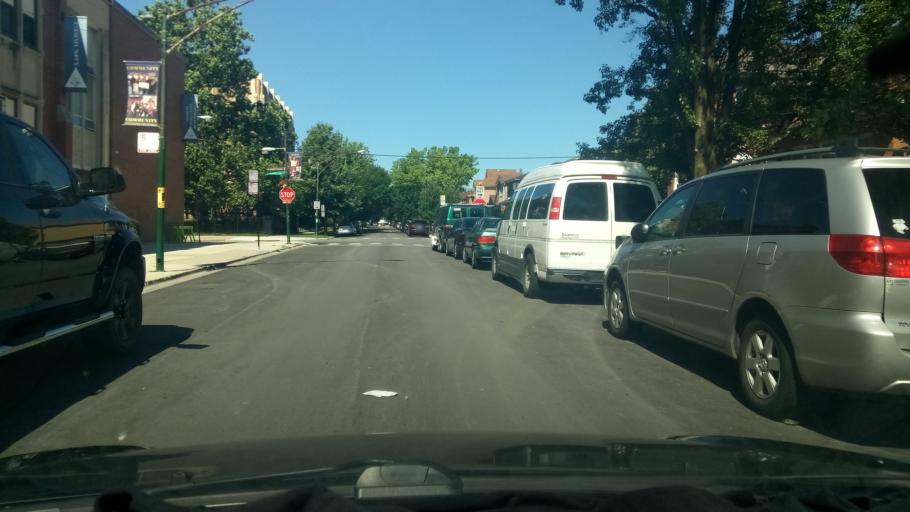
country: US
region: Illinois
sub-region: Cook County
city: Hometown
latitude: 41.7805
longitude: -87.7173
